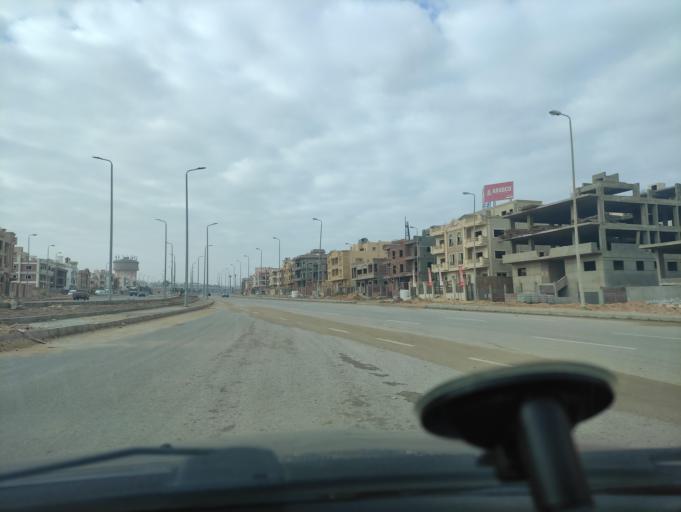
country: EG
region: Muhafazat al Qalyubiyah
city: Al Khankah
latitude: 30.0508
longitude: 31.5310
